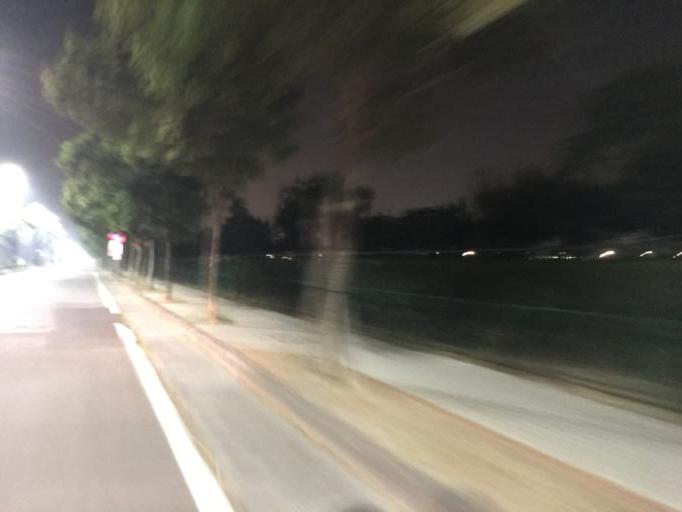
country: TW
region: Taiwan
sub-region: Chiayi
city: Taibao
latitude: 23.4779
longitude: 120.2986
